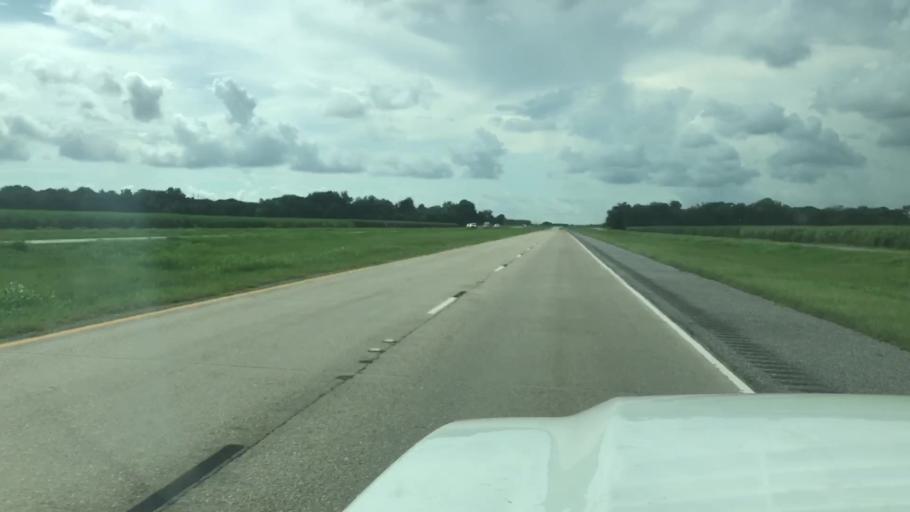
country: US
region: Louisiana
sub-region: Saint Mary Parish
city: Franklin
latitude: 29.7625
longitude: -91.4821
